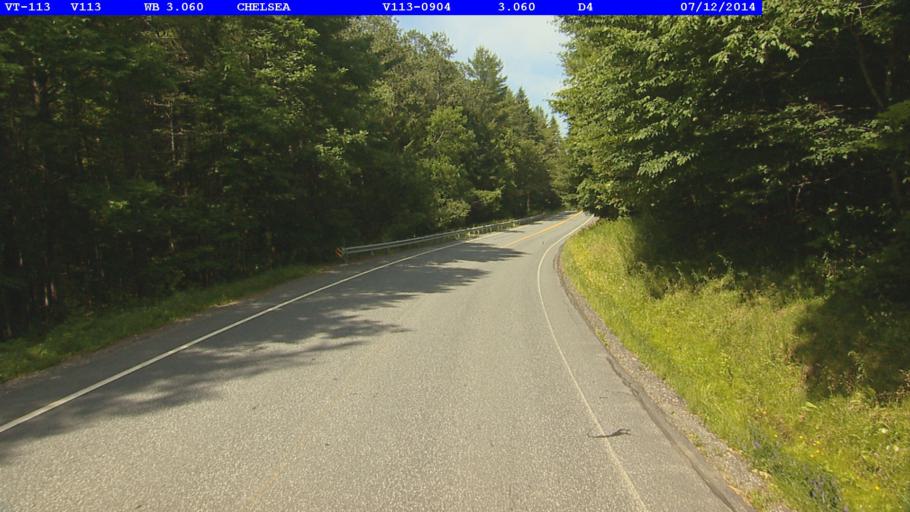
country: US
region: Vermont
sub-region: Orange County
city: Chelsea
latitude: 43.9923
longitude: -72.3919
